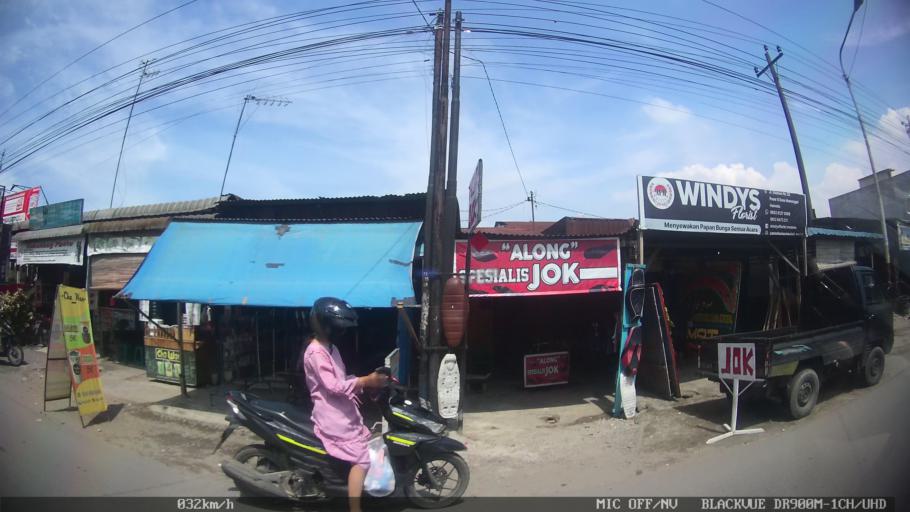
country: ID
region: North Sumatra
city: Labuhan Deli
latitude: 3.6601
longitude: 98.6565
